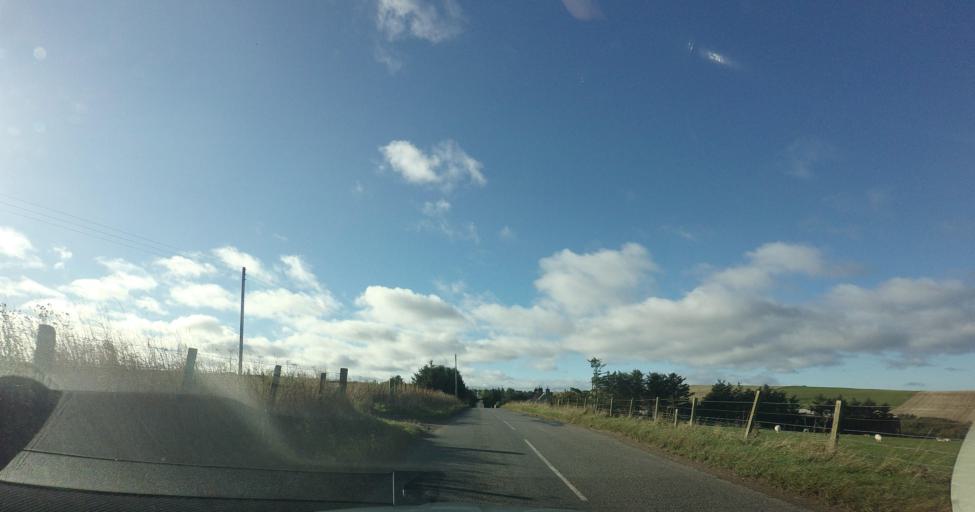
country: GB
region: Scotland
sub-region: Aberdeenshire
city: Macduff
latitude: 57.6652
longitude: -2.3139
